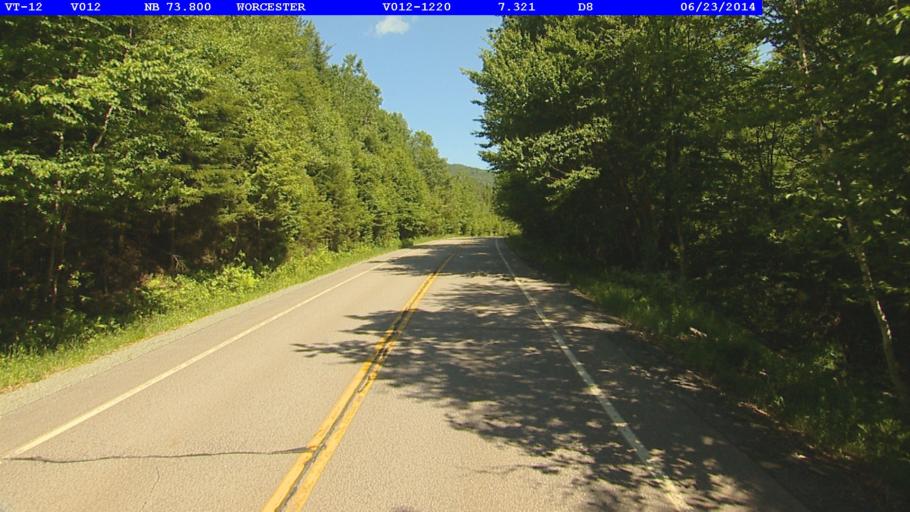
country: US
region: Vermont
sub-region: Lamoille County
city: Morrisville
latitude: 44.4446
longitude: -72.5441
